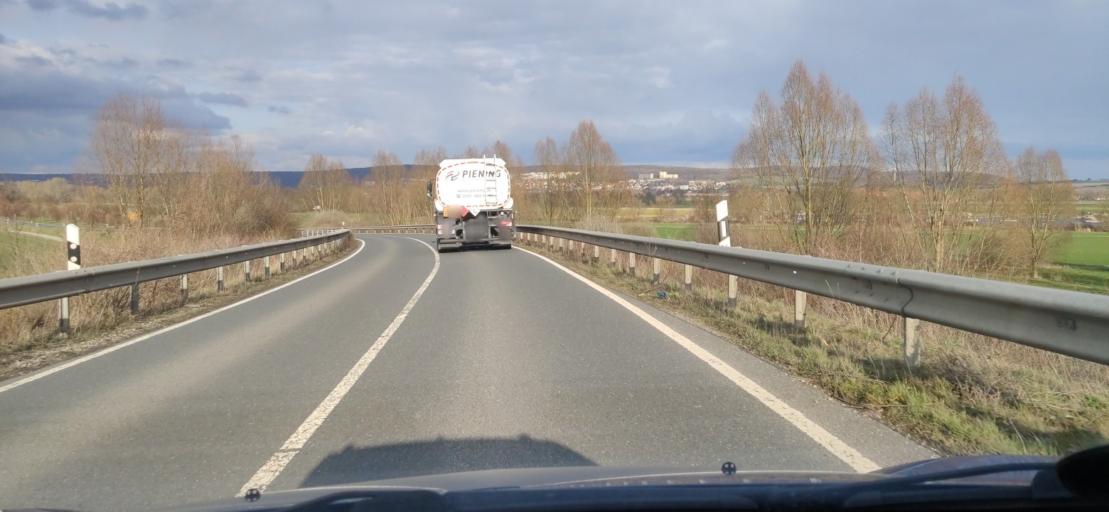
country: DE
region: Lower Saxony
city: Rosdorf
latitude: 51.4959
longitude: 9.9095
